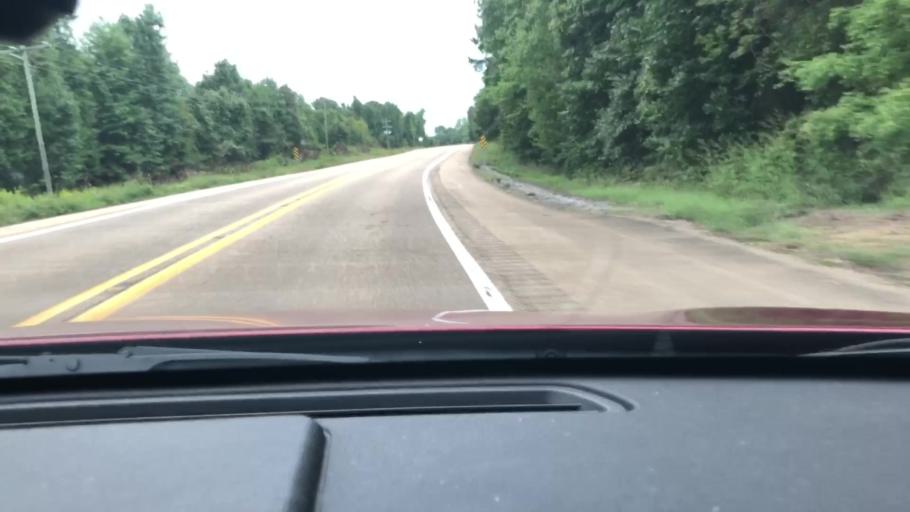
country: US
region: Arkansas
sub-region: Miller County
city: Texarkana
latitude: 33.4178
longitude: -93.8138
